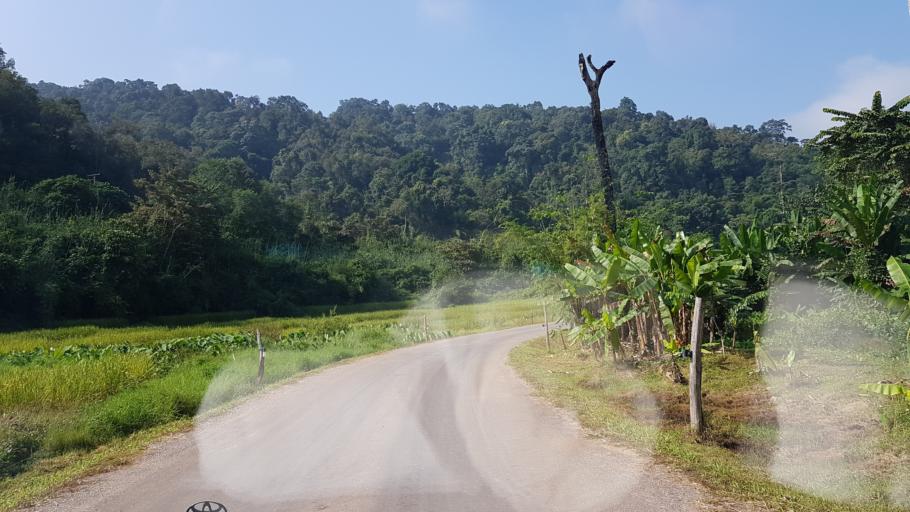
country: LA
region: Oudomxai
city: Muang Xay
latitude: 20.7155
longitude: 102.0970
